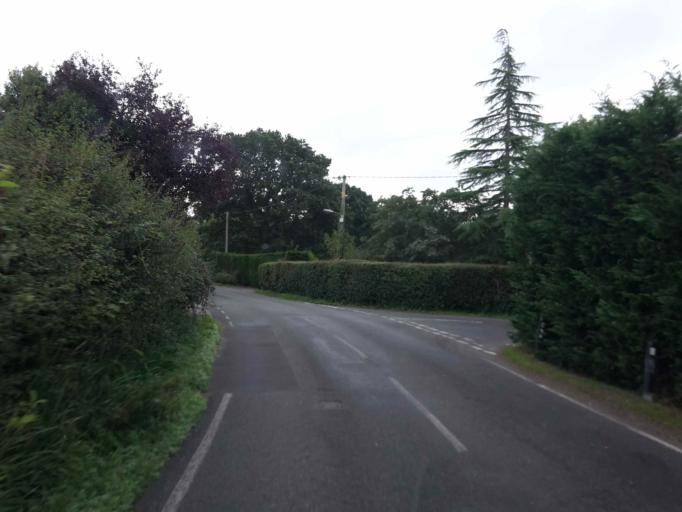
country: GB
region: England
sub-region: West Sussex
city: Rudgwick
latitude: 51.0646
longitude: -0.4471
